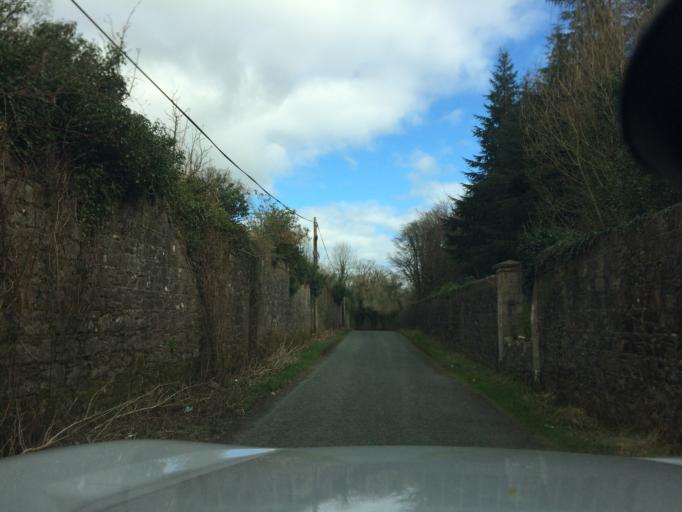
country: IE
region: Munster
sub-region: Waterford
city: Portlaw
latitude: 52.2865
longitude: -7.3340
